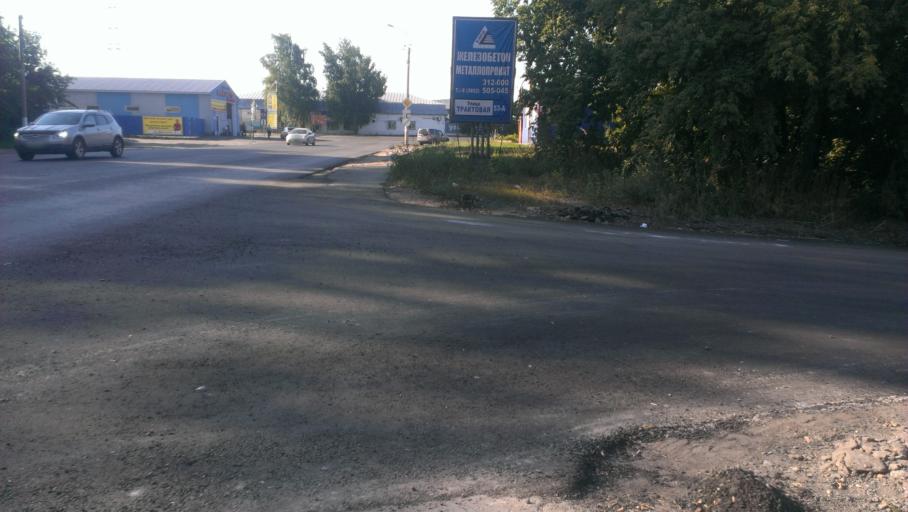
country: RU
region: Altai Krai
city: Novosilikatnyy
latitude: 53.3106
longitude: 83.6211
